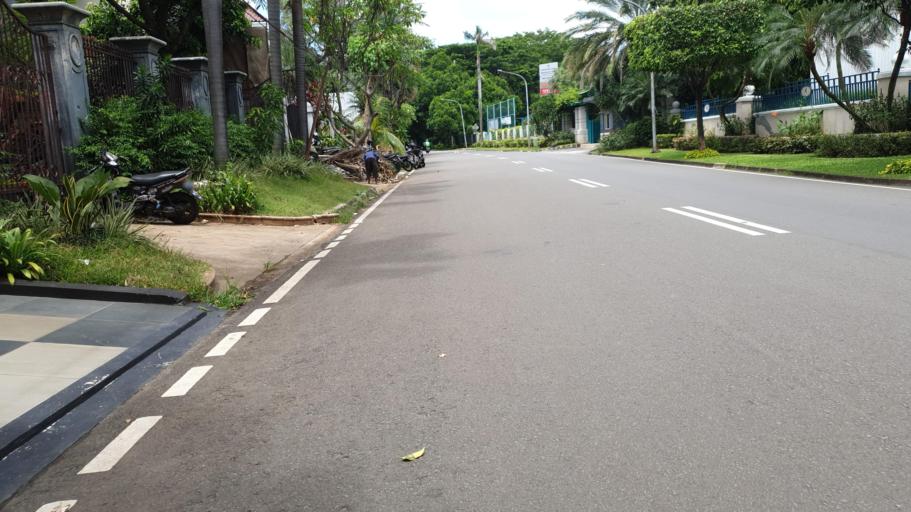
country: ID
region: Banten
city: South Tangerang
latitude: -6.2756
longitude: 106.7846
